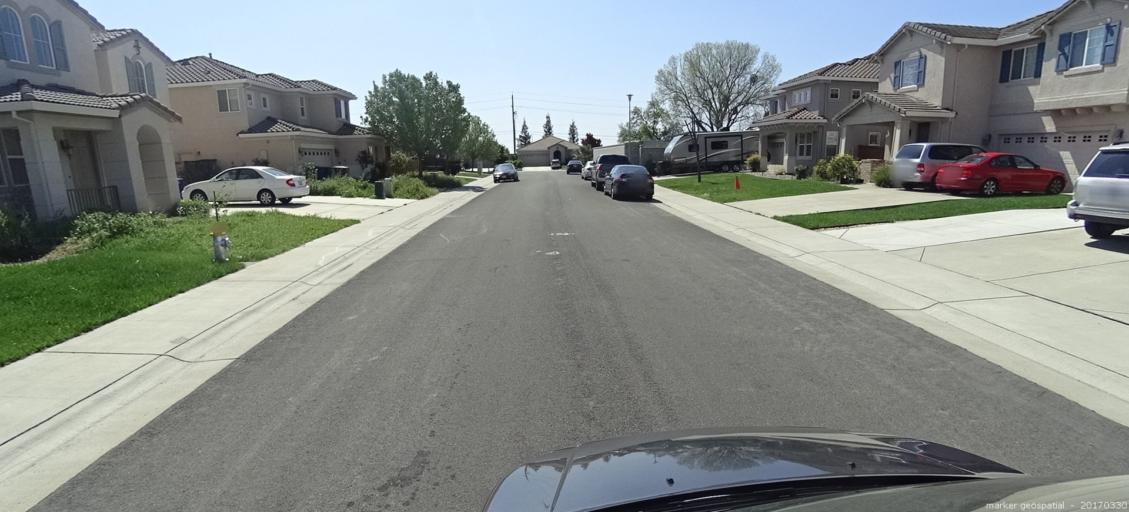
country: US
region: California
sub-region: Sacramento County
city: Laguna
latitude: 38.4395
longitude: -121.4123
